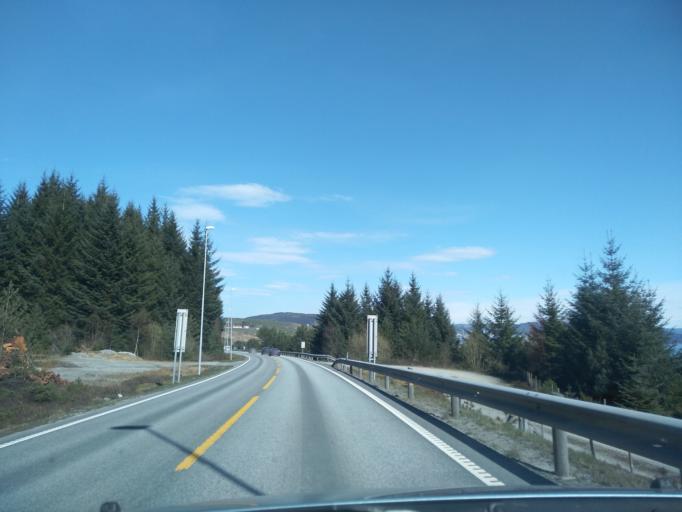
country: NO
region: Rogaland
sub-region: Bokn
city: Bokn
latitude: 59.2442
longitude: 5.4722
